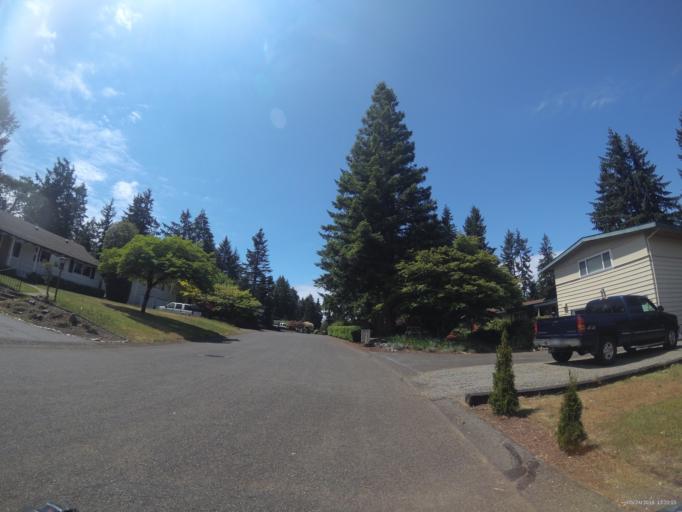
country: US
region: Washington
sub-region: Pierce County
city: Lakewood
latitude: 47.1832
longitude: -122.5259
